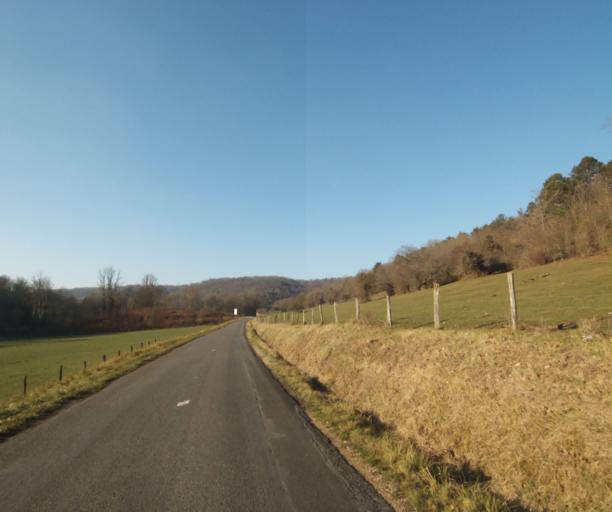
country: FR
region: Champagne-Ardenne
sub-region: Departement de la Haute-Marne
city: Chevillon
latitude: 48.5017
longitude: 5.1799
